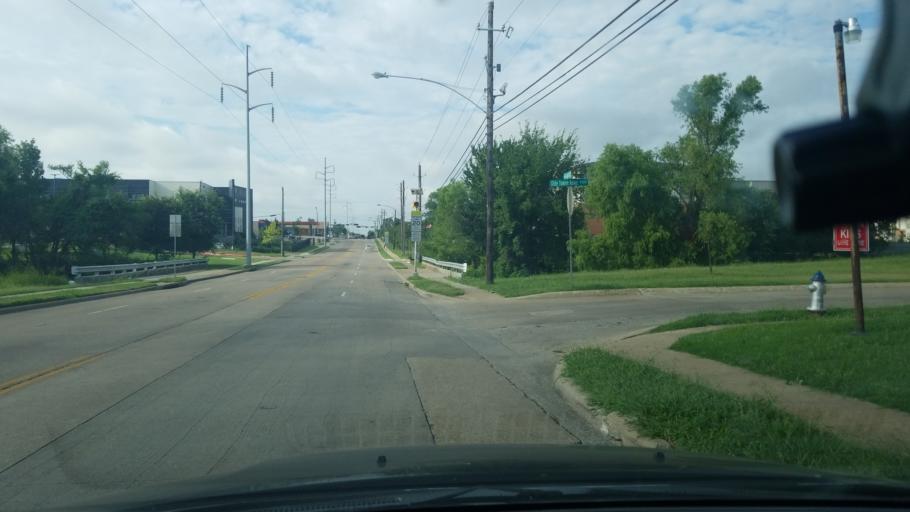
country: US
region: Texas
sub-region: Dallas County
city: Balch Springs
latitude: 32.7517
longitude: -96.6569
